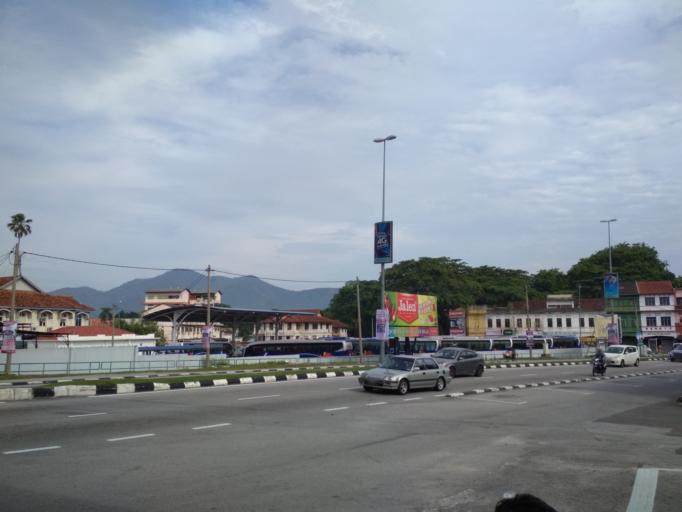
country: MY
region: Perak
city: Ipoh
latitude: 4.5896
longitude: 101.0830
